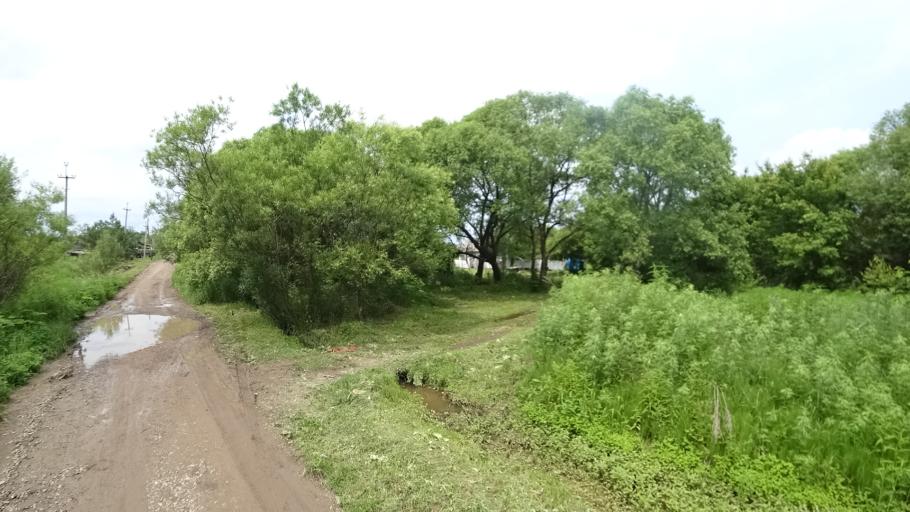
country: RU
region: Primorskiy
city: Novosysoyevka
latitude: 44.2278
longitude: 133.3715
